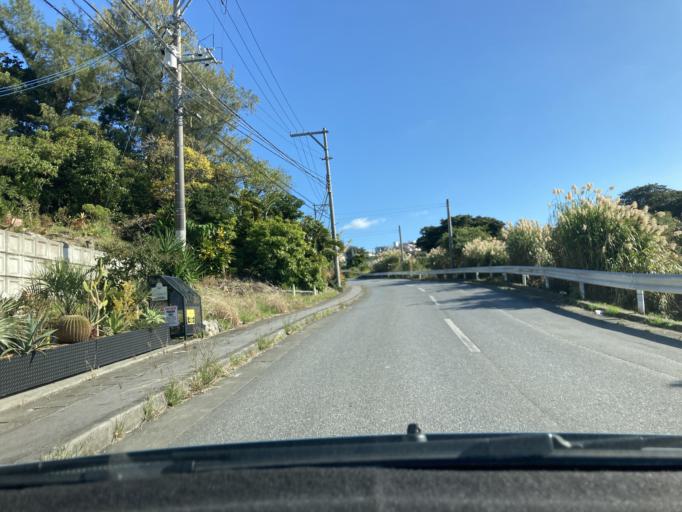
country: JP
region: Okinawa
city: Chatan
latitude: 26.2912
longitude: 127.7933
